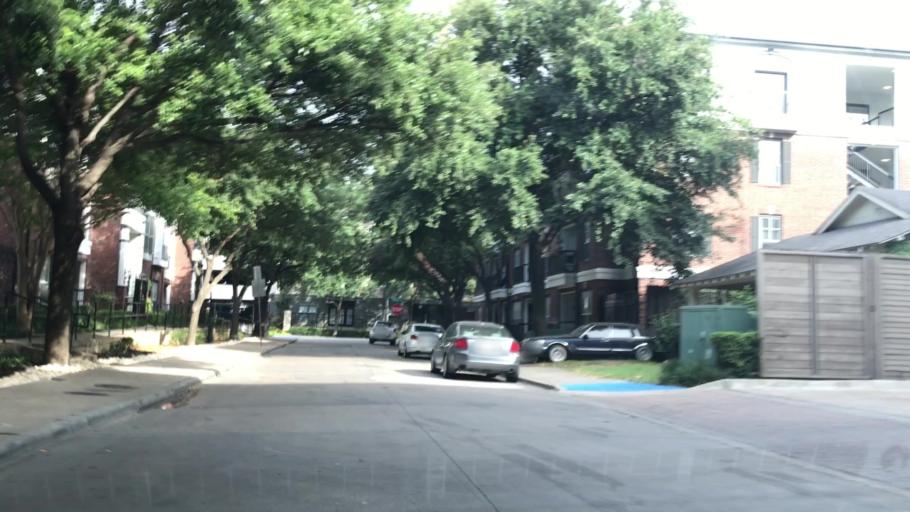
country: US
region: Texas
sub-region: Dallas County
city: Dallas
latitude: 32.7911
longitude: -96.7902
